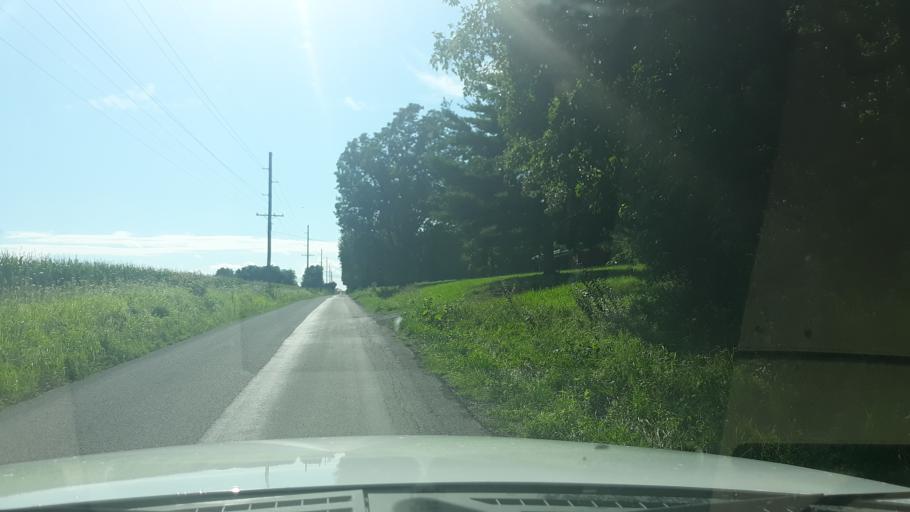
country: US
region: Illinois
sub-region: Saline County
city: Eldorado
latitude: 37.8630
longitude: -88.5325
